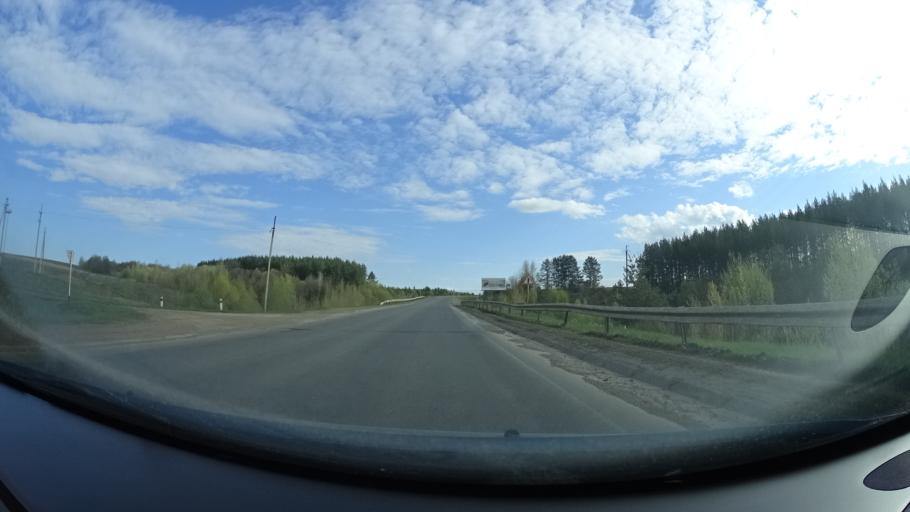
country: RU
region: Bashkortostan
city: Blagoveshchensk
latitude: 55.0846
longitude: 55.8079
